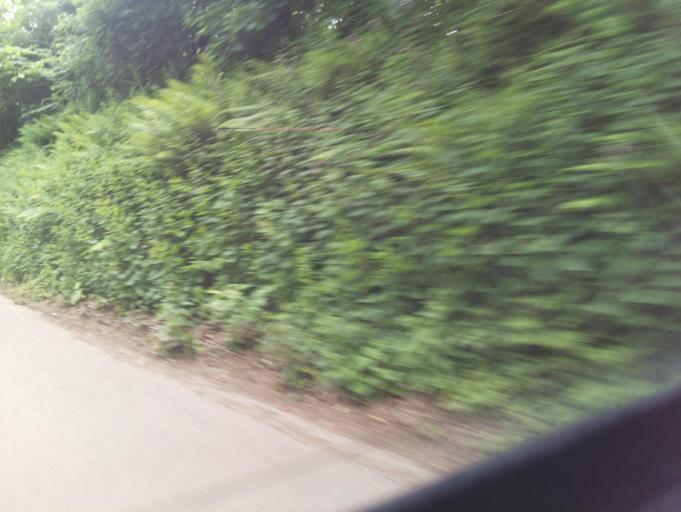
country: GB
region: England
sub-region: Devon
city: Totnes
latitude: 50.4218
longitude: -3.6943
